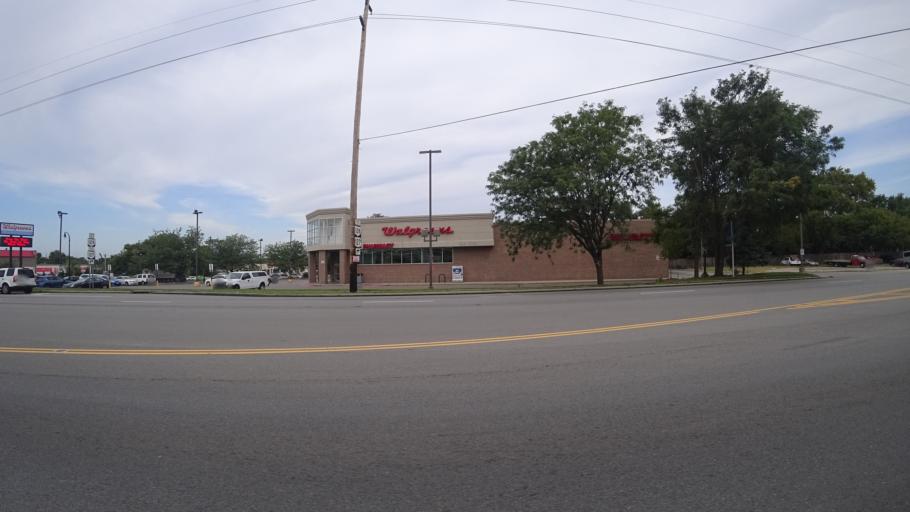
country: US
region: Ohio
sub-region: Butler County
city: Hamilton
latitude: 39.3964
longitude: -84.5482
